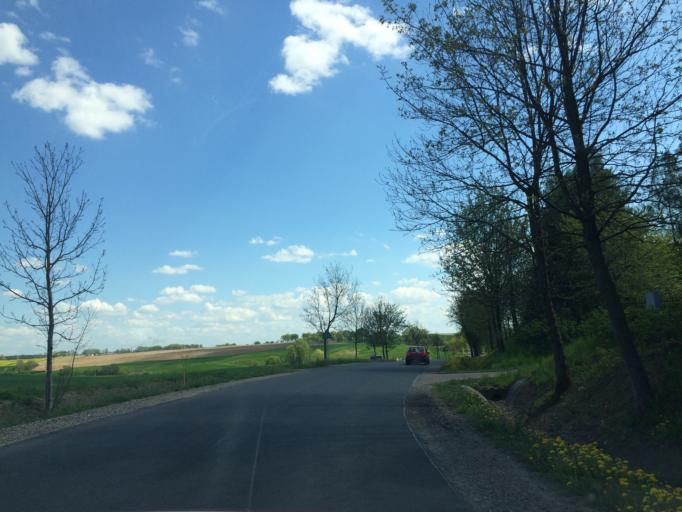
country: PL
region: Warmian-Masurian Voivodeship
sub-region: Powiat nowomiejski
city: Nowe Miasto Lubawskie
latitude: 53.4036
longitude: 19.6104
